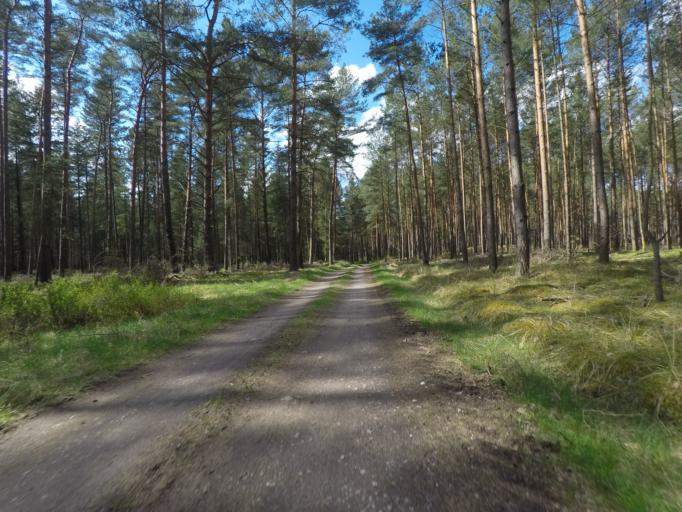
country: DE
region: Brandenburg
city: Melchow
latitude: 52.8225
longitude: 13.6737
